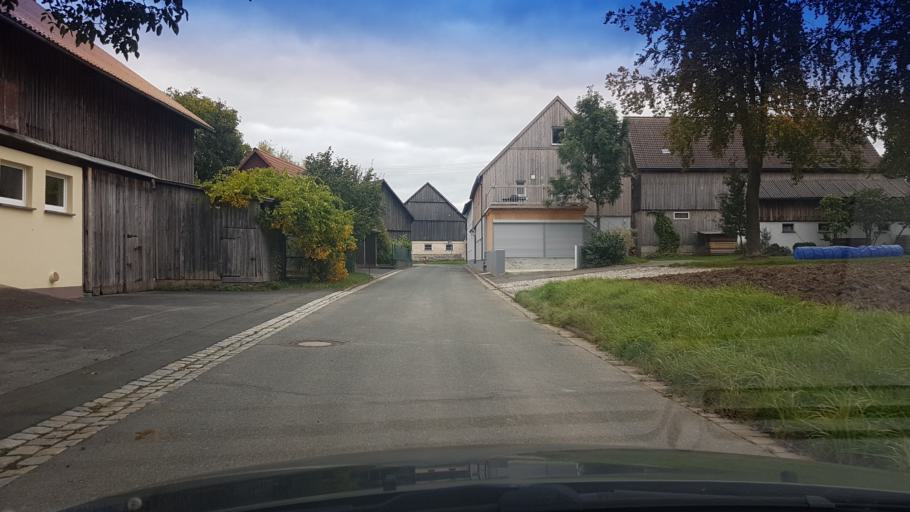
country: DE
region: Bavaria
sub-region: Upper Franconia
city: Wonsees
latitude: 50.0112
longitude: 11.2570
